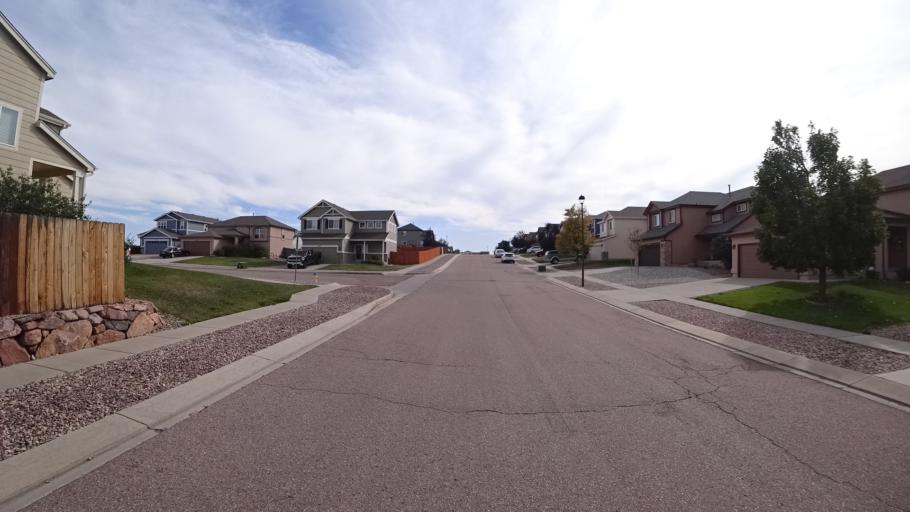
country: US
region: Colorado
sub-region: El Paso County
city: Cimarron Hills
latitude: 38.9085
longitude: -104.6871
